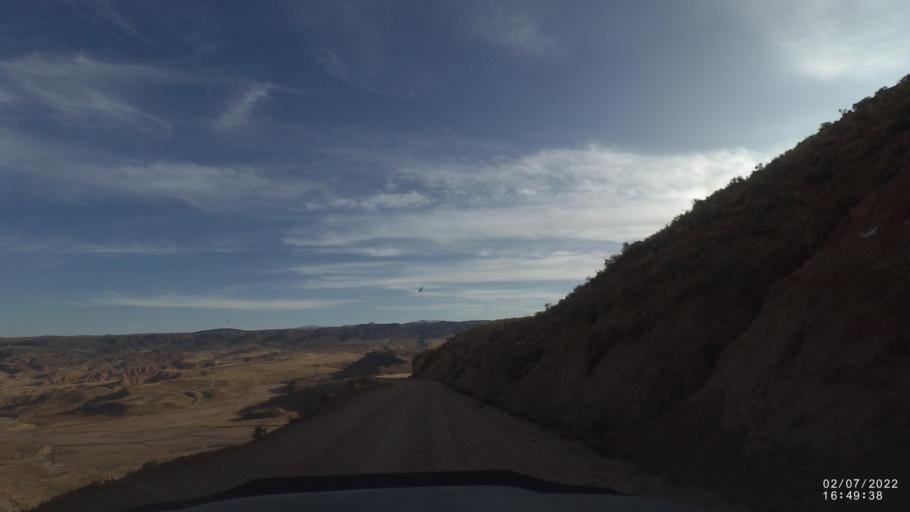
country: BO
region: Cochabamba
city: Irpa Irpa
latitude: -17.9746
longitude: -66.5275
